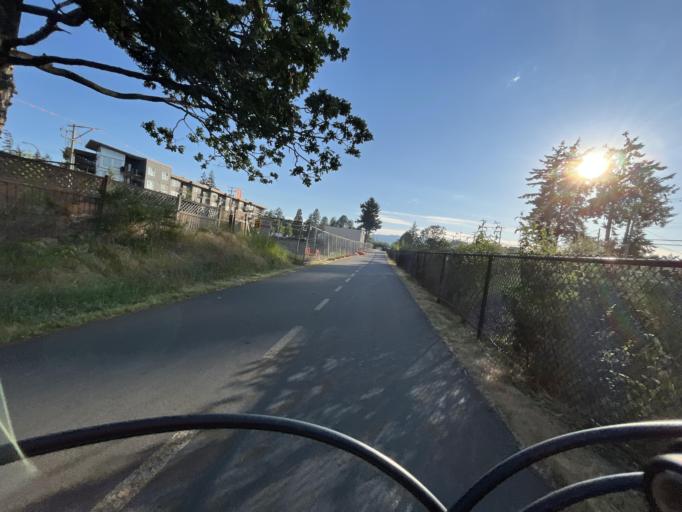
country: CA
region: British Columbia
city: Langford
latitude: 48.4479
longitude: -123.4922
